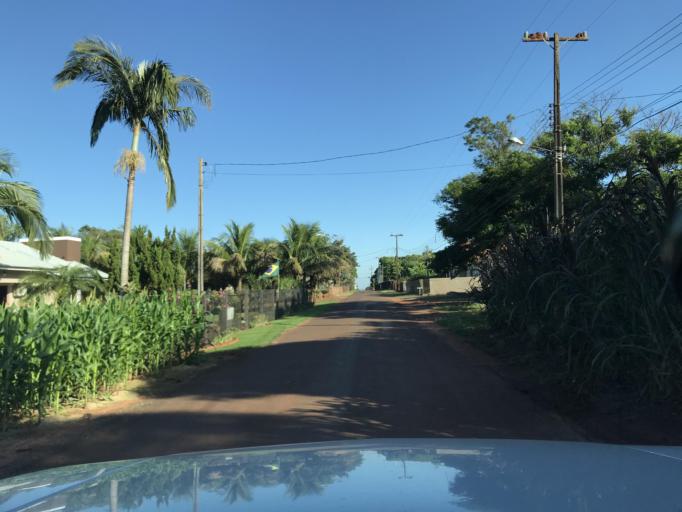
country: BR
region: Parana
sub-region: Palotina
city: Palotina
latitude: -24.2336
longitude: -53.7822
